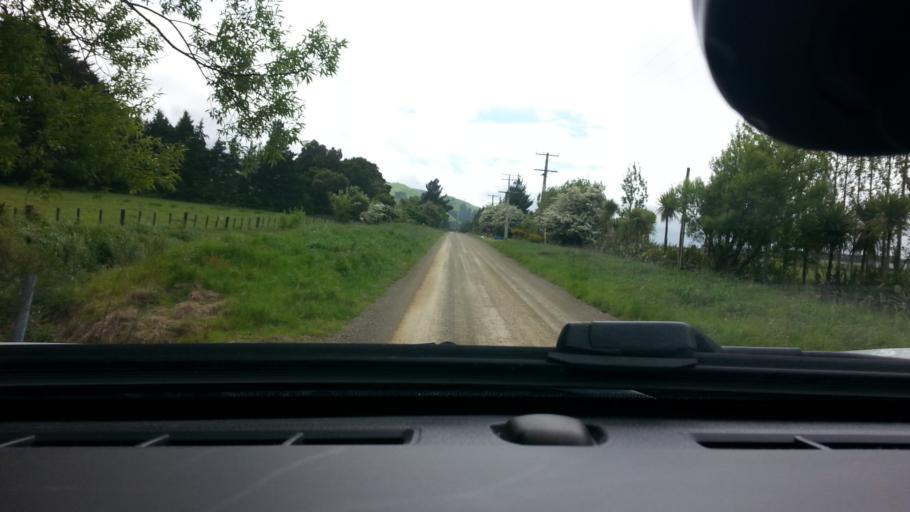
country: NZ
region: Wellington
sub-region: Upper Hutt City
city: Upper Hutt
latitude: -41.0899
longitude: 175.3486
